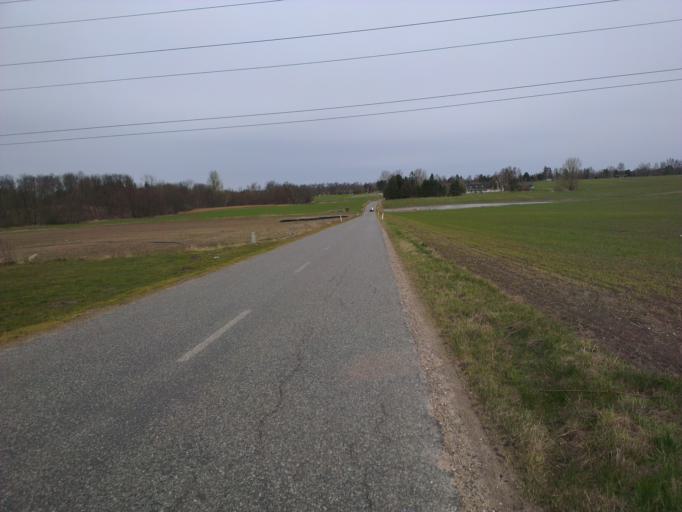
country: DK
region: Capital Region
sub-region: Frederikssund Kommune
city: Jaegerspris
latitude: 55.8056
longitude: 11.9318
